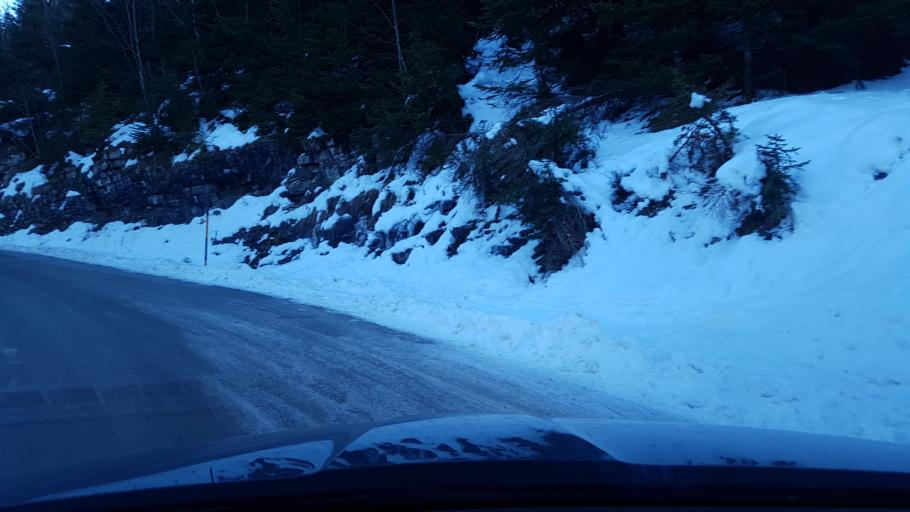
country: AT
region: Salzburg
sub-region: Politischer Bezirk Hallein
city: Scheffau am Tennengebirge
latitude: 47.6441
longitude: 13.2387
